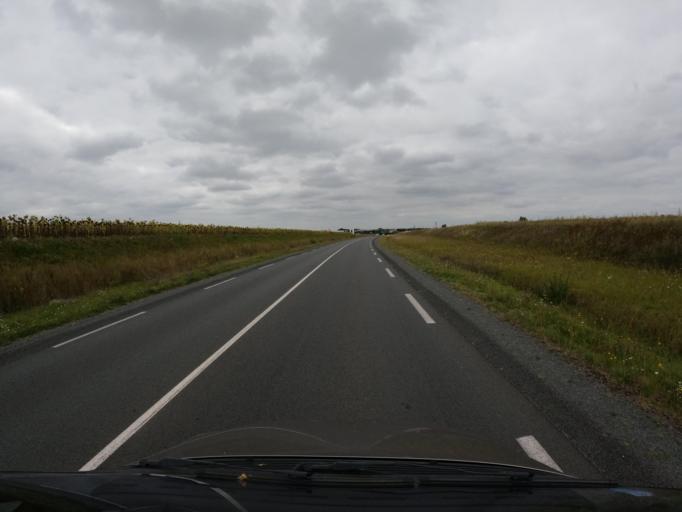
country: FR
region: Pays de la Loire
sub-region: Departement de la Vendee
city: Fontenay-le-Comte
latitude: 46.4436
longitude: -0.8030
